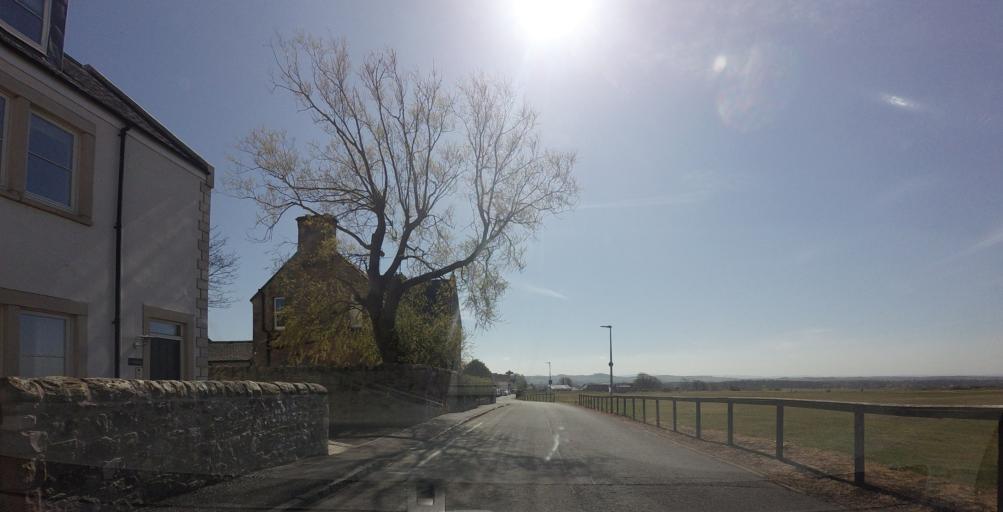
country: GB
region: Scotland
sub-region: East Lothian
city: Gullane
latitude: 56.0341
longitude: -2.8306
